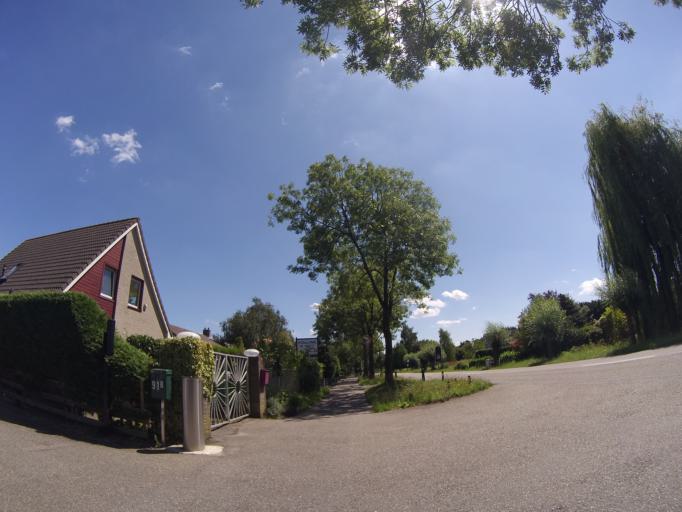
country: NL
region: Utrecht
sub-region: Stichtse Vecht
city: Maarssen
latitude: 52.1345
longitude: 5.0906
